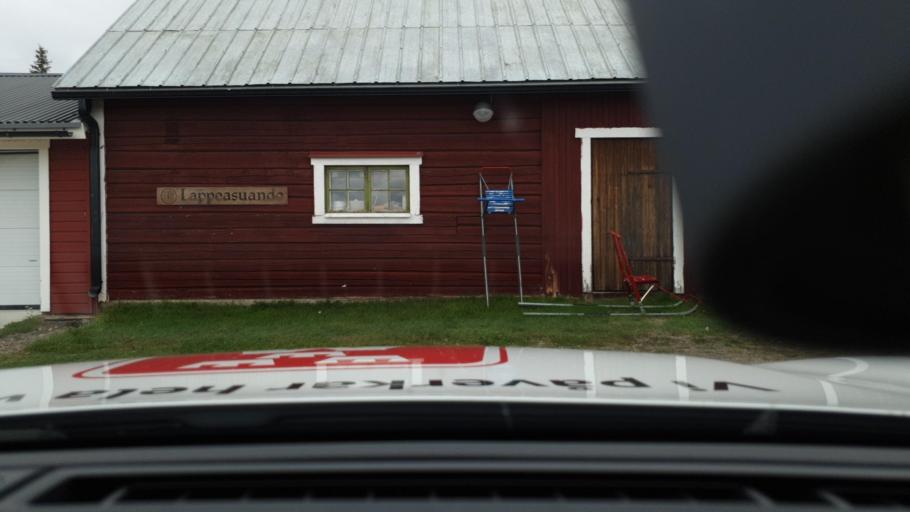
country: SE
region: Norrbotten
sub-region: Gallivare Kommun
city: Malmberget
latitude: 67.4909
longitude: 21.1185
